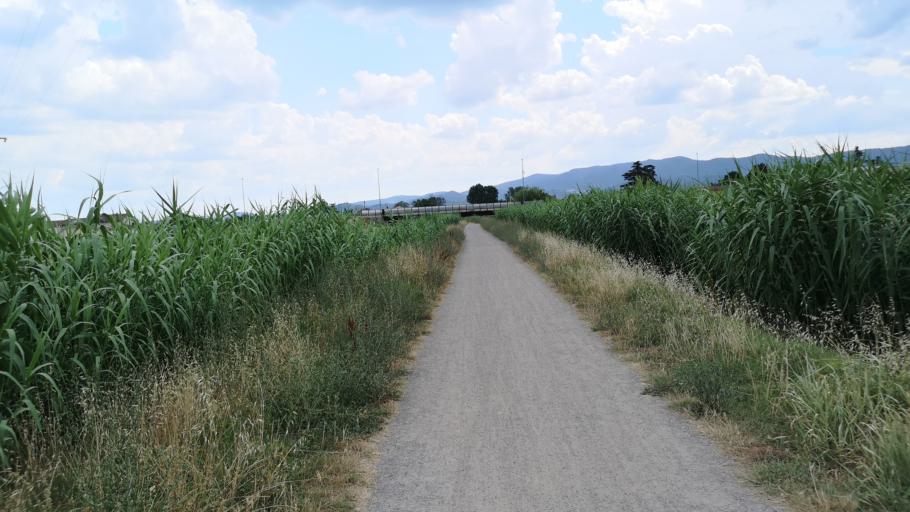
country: IT
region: Tuscany
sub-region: Provincia di Prato
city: Fornacelle
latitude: 43.8803
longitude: 11.0479
